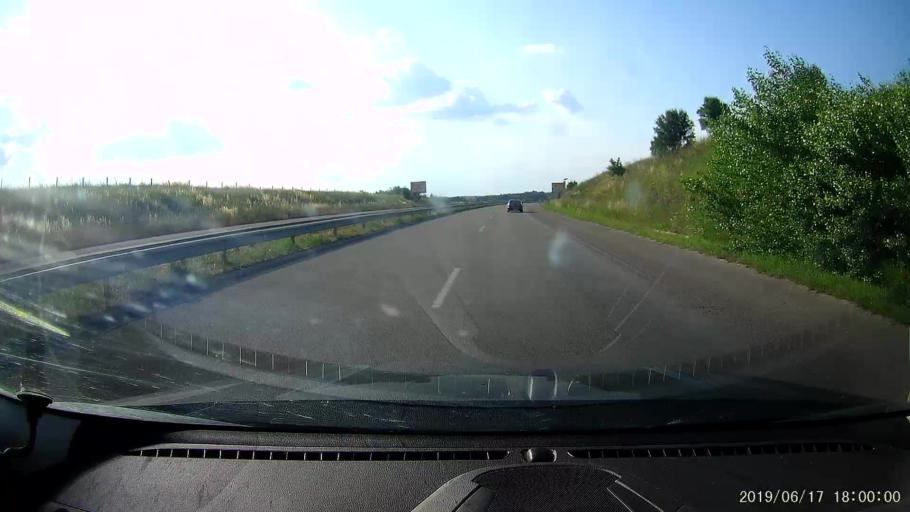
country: BG
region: Khaskovo
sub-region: Obshtina Svilengrad
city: Svilengrad
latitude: 41.7296
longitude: 26.2854
